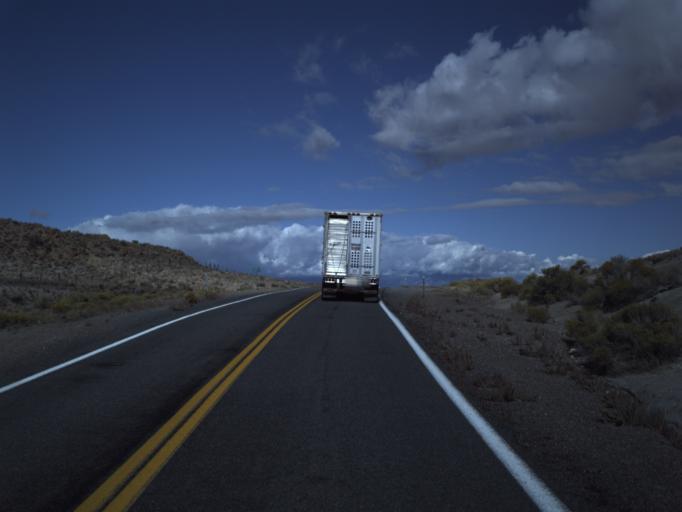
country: US
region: Utah
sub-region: Beaver County
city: Milford
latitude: 38.6163
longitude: -113.8433
